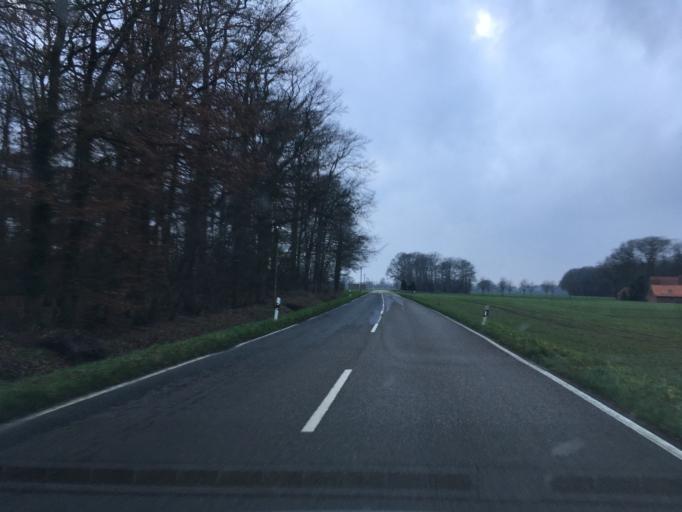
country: DE
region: North Rhine-Westphalia
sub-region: Regierungsbezirk Munster
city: Heek
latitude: 52.1754
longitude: 7.0901
